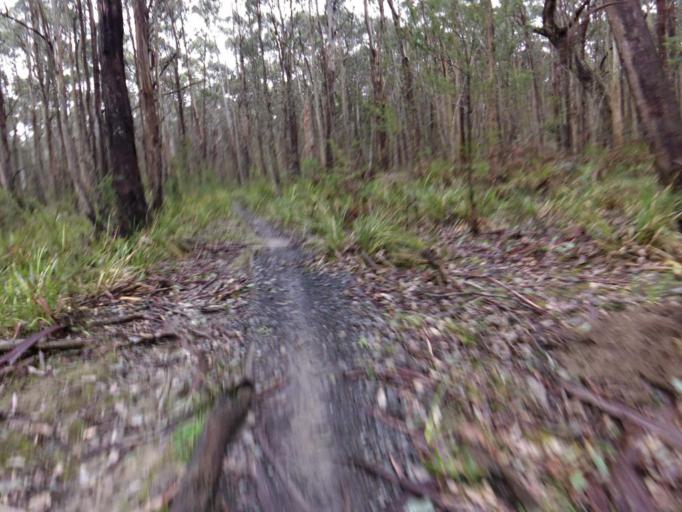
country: AU
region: Victoria
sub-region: Moorabool
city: Bacchus Marsh
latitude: -37.4142
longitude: 144.4907
